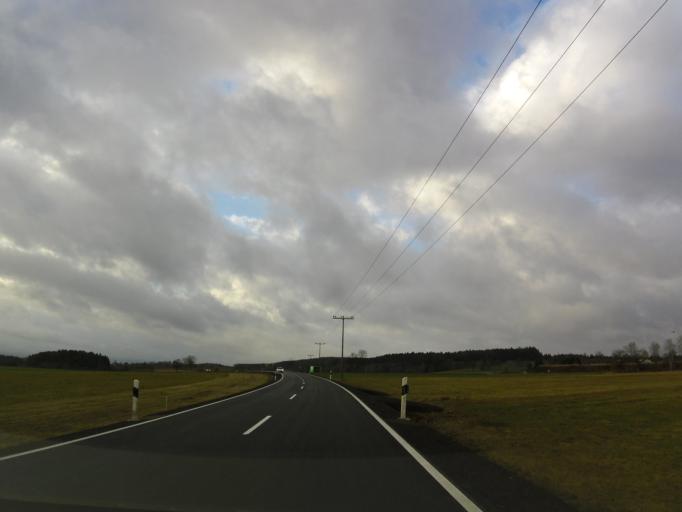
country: DE
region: Bavaria
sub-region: Upper Franconia
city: Hochstadt bei Thiersheim
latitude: 50.0756
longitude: 12.0800
